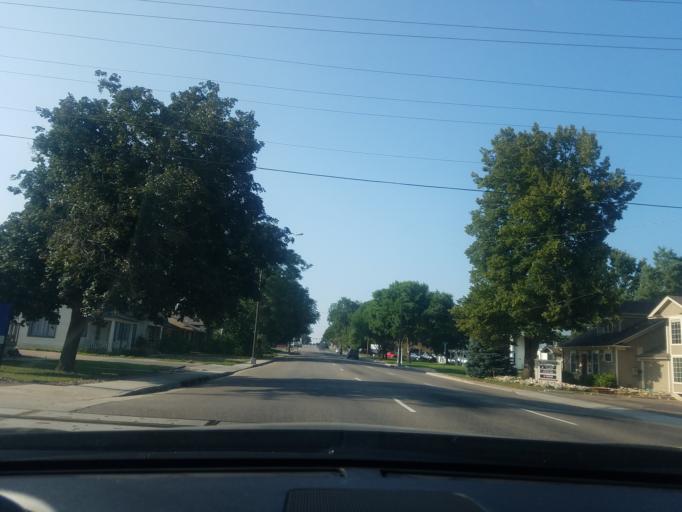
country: US
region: Colorado
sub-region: Larimer County
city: Loveland
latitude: 40.4026
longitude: -105.0732
